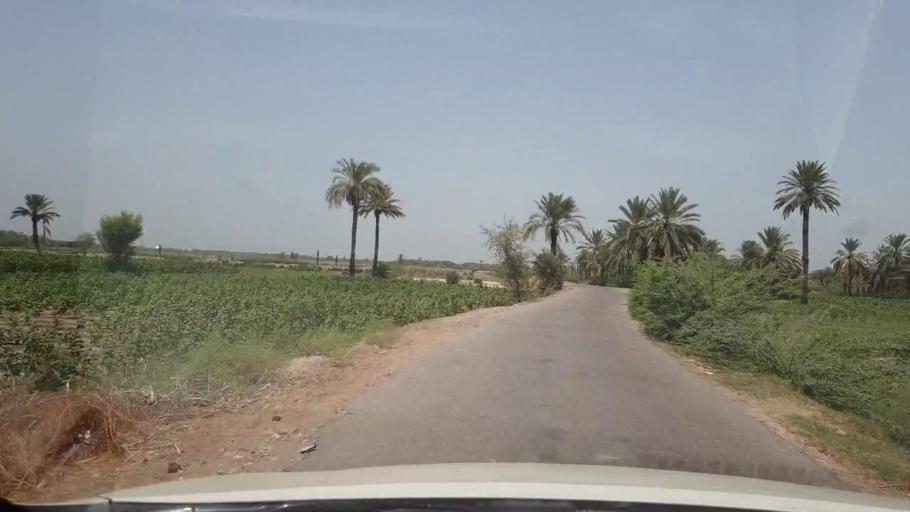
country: PK
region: Sindh
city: Bozdar
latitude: 27.2493
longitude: 68.6510
